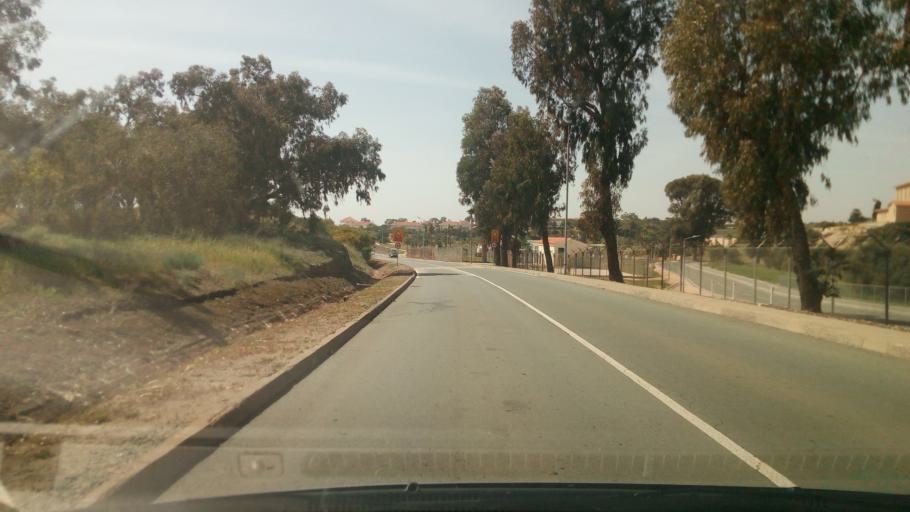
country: CY
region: Larnaka
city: Xylotymbou
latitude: 34.9837
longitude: 33.7372
